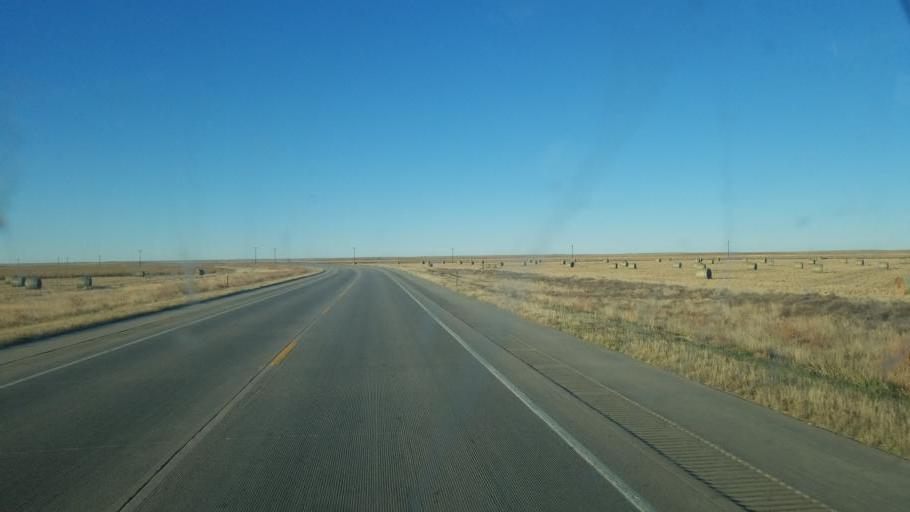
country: US
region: Colorado
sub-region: Kiowa County
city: Eads
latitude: 38.6835
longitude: -102.7816
